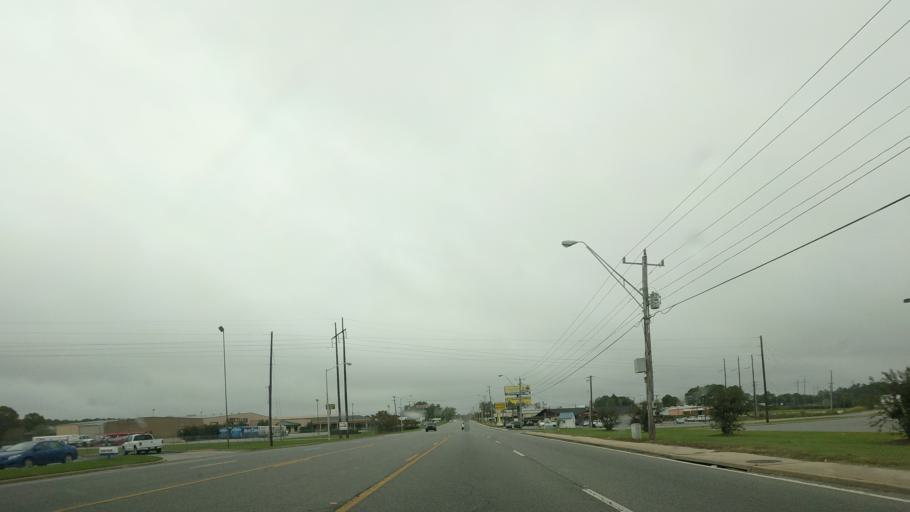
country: US
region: Georgia
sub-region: Ben Hill County
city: Fitzgerald
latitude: 31.6943
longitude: -83.2463
